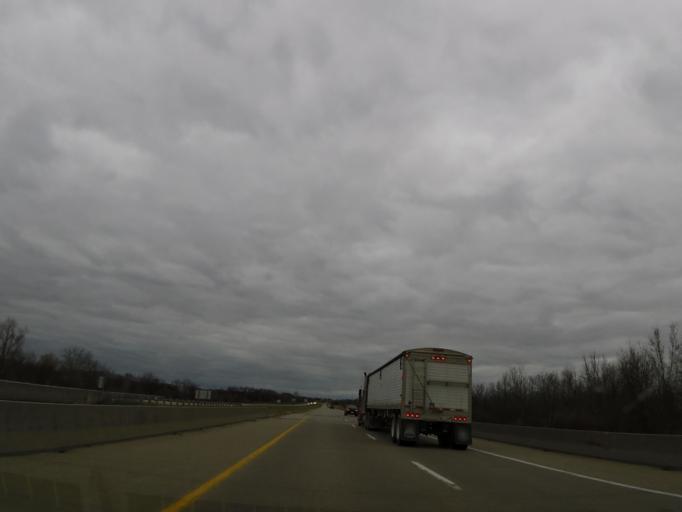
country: US
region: Iowa
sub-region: Johnson County
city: Lone Tree
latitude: 41.4782
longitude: -91.5509
